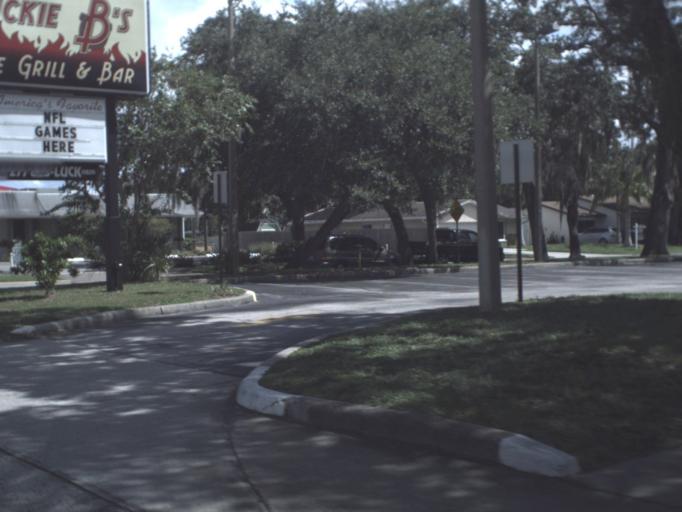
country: US
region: Florida
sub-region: Pinellas County
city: Lealman
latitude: 27.8118
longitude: -82.6385
